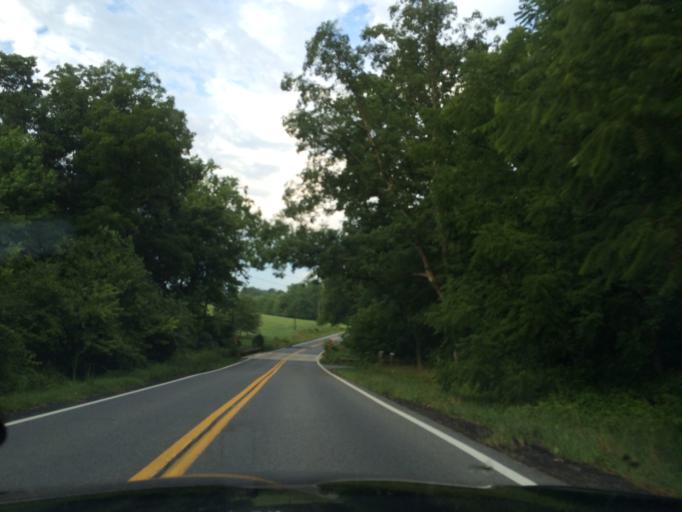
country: US
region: Maryland
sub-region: Frederick County
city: Green Valley
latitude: 39.3056
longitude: -77.2516
